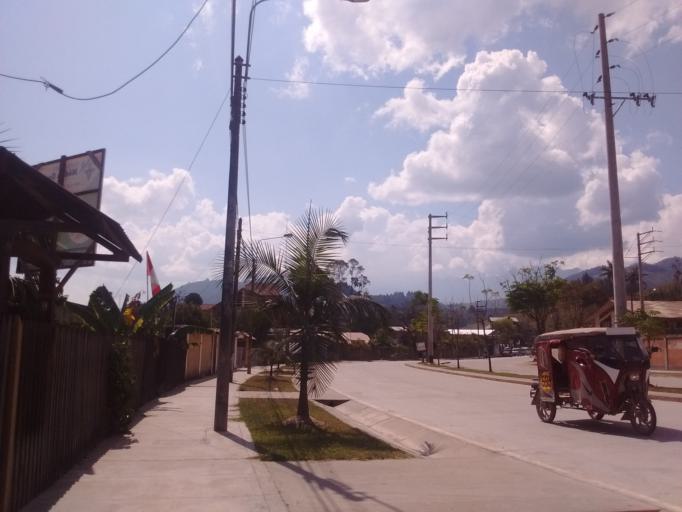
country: PE
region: Pasco
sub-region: Provincia de Oxapampa
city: Oxapampa
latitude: -10.5712
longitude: -75.4074
